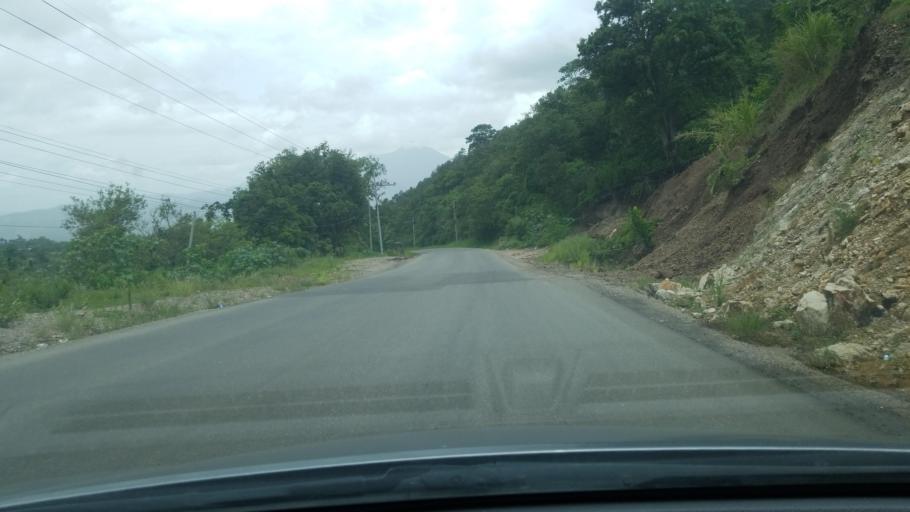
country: HN
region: Copan
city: Ojos de Agua
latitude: 14.6737
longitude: -88.8312
